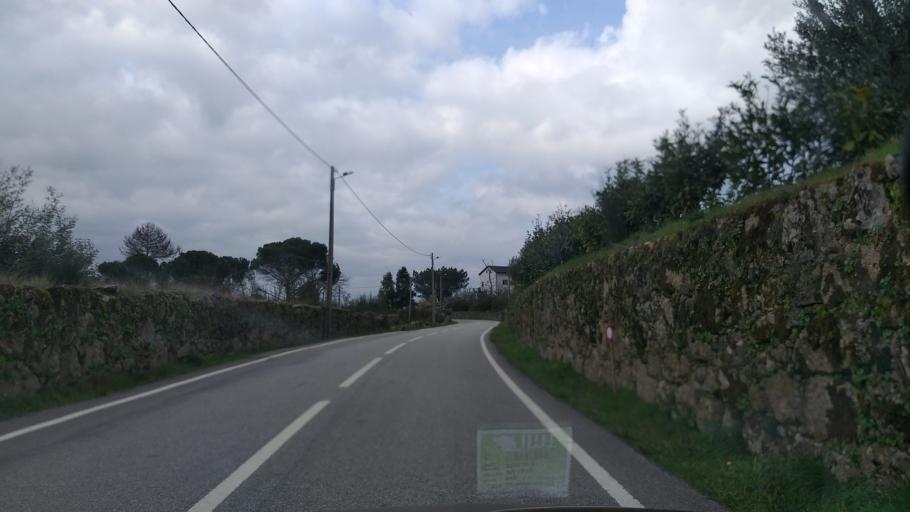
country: PT
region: Guarda
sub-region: Seia
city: Seia
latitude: 40.4860
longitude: -7.6326
